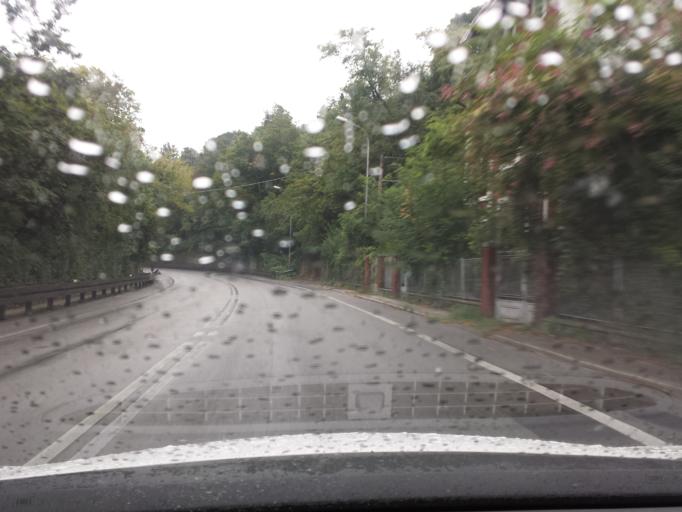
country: IT
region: Friuli Venezia Giulia
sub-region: Provincia di Trieste
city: Prosecco-Contovello
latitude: 45.7093
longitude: 13.7152
